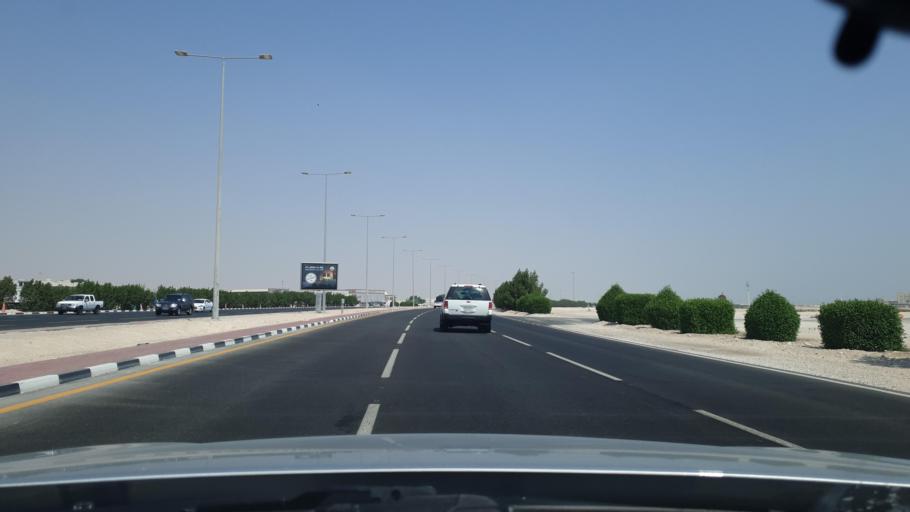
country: QA
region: Al Khawr
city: Al Khawr
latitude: 25.7087
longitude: 51.5055
